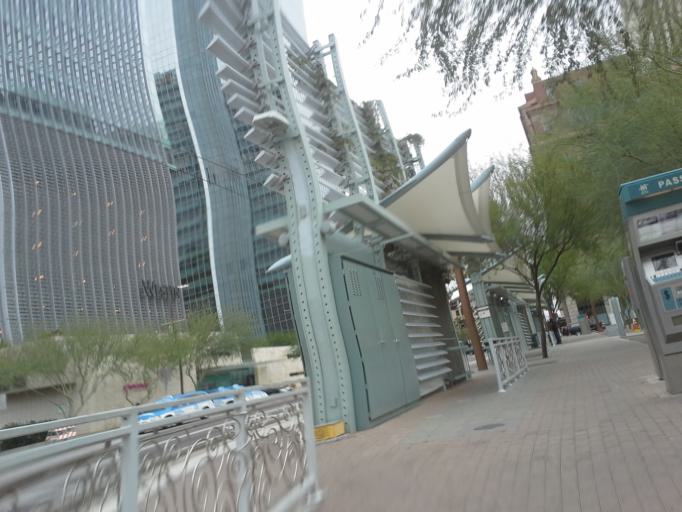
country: US
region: Arizona
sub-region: Maricopa County
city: Phoenix
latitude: 33.4524
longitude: -112.0740
